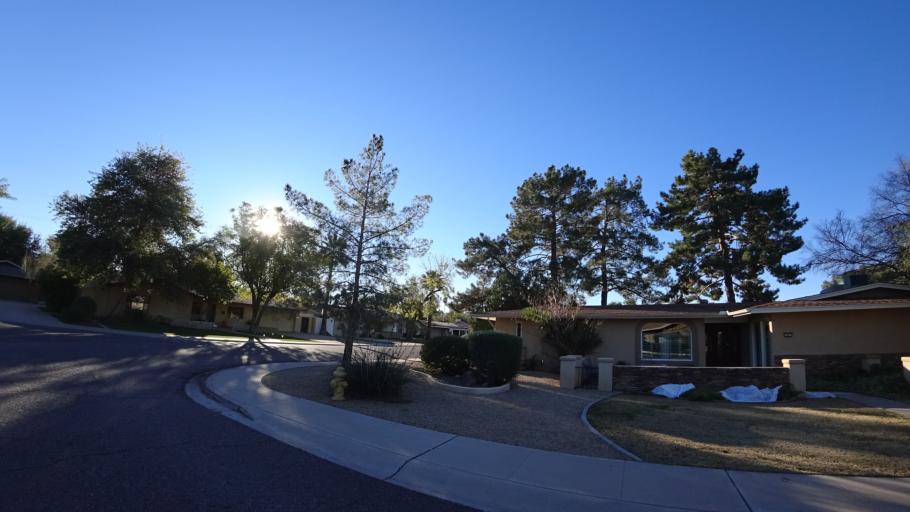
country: US
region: Arizona
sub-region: Maricopa County
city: Paradise Valley
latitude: 33.5040
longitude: -112.0071
